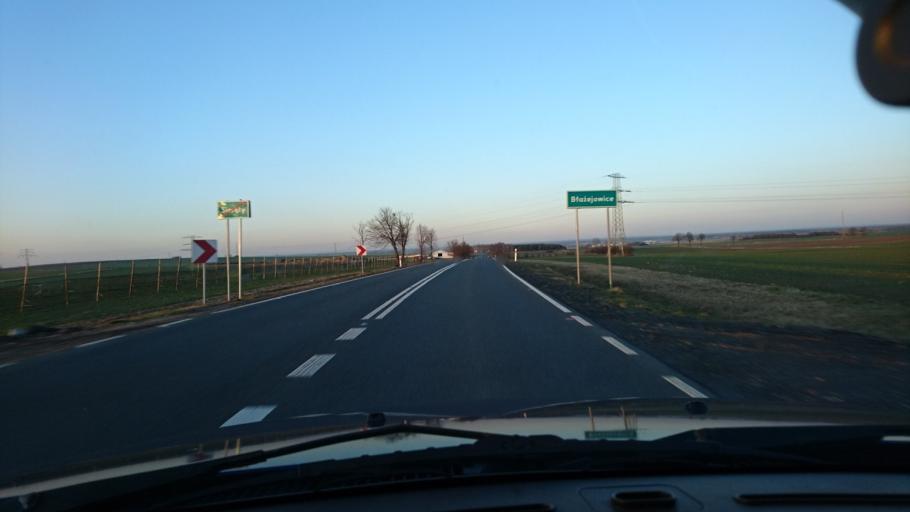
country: PL
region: Silesian Voivodeship
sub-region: Powiat gliwicki
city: Wielowies
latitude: 50.4857
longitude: 18.6046
